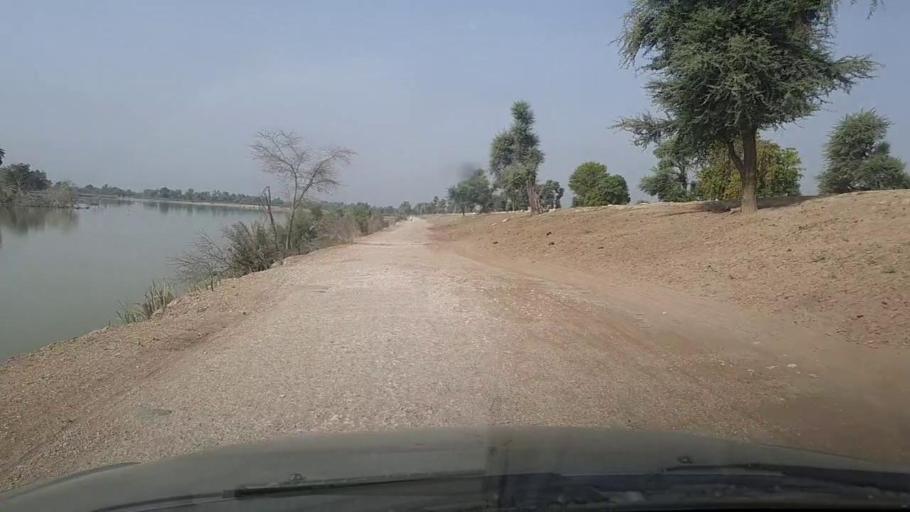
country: PK
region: Sindh
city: Pir jo Goth
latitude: 27.5211
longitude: 68.4837
